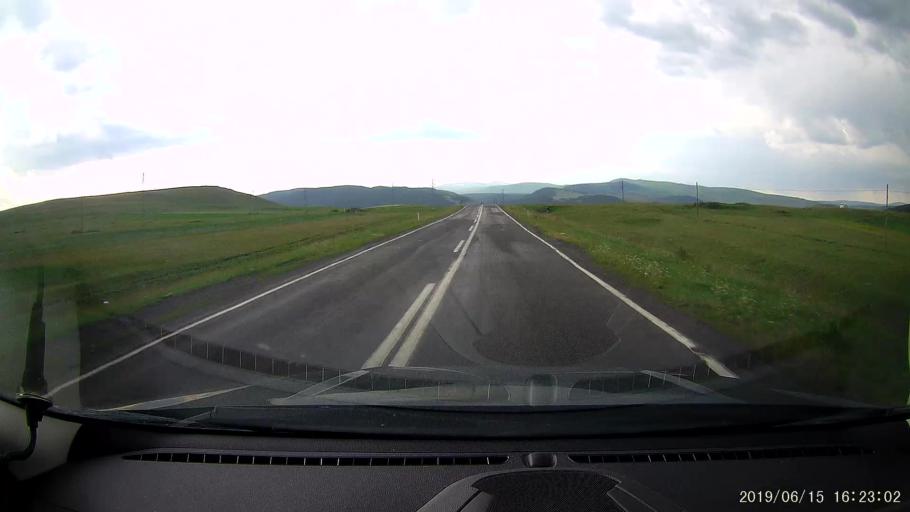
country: TR
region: Ardahan
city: Hanak
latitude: 41.1819
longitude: 42.8570
